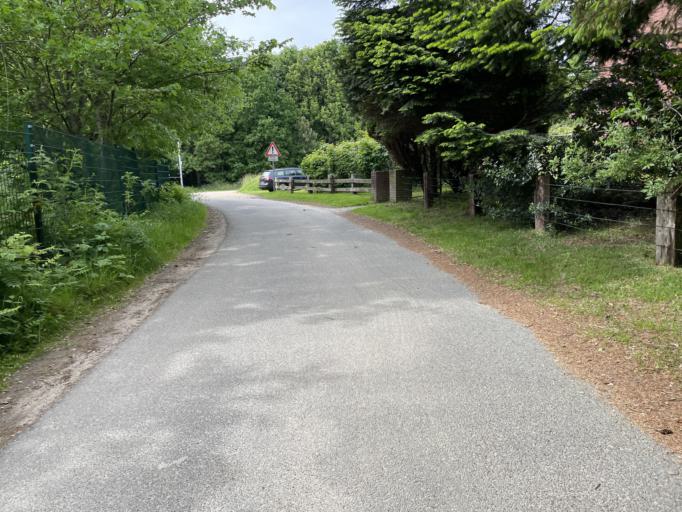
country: DE
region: Schleswig-Holstein
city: Husum
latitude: 54.4715
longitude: 9.0681
